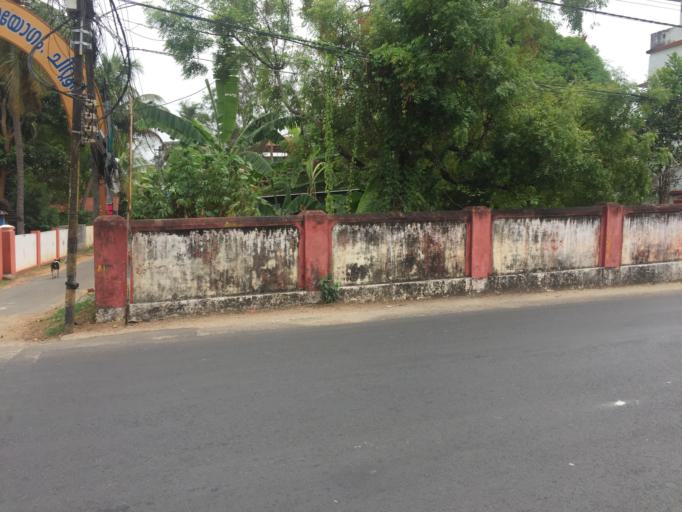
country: IN
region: Kerala
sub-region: Palakkad district
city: Chittur
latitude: 10.7012
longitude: 76.7412
